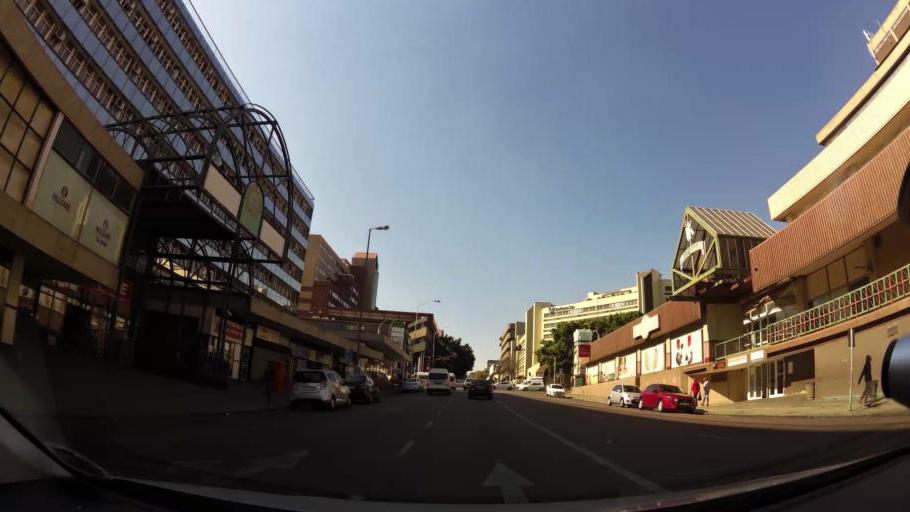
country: ZA
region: Gauteng
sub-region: City of Tshwane Metropolitan Municipality
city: Pretoria
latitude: -25.7454
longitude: 28.2032
